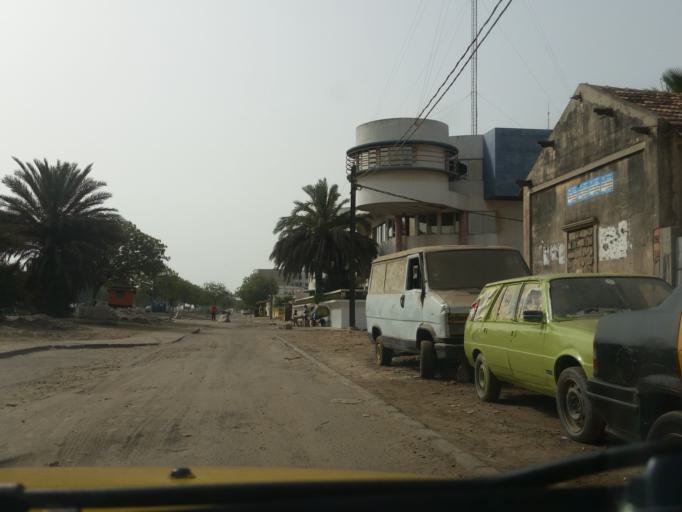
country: SN
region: Dakar
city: Pikine
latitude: 14.7133
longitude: -17.2697
